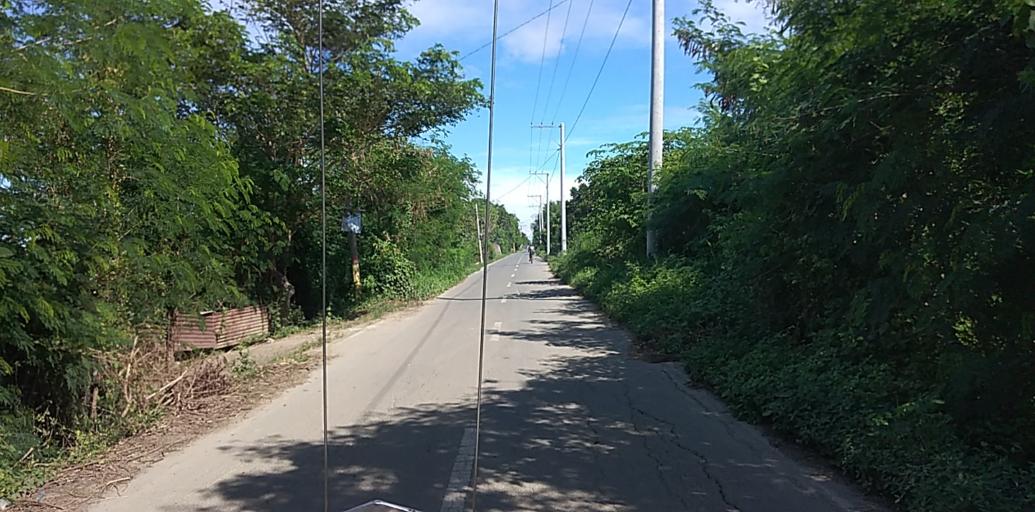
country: PH
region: Central Luzon
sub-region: Province of Pampanga
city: Candaba
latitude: 15.0808
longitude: 120.8089
